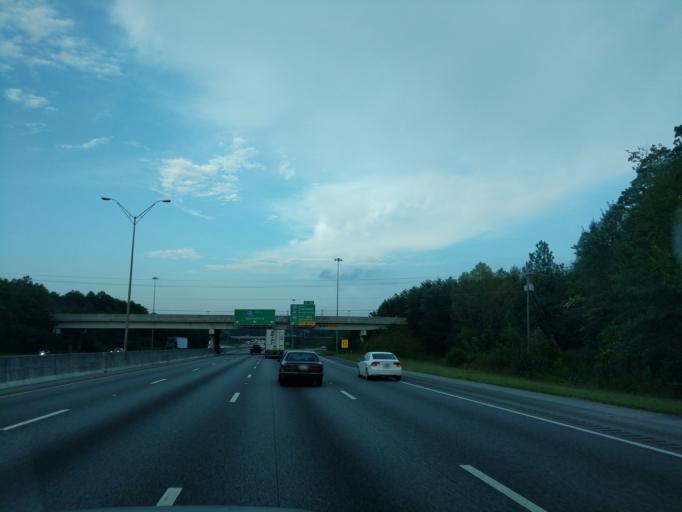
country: US
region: South Carolina
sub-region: Greenville County
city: Gantt
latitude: 34.7859
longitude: -82.4474
